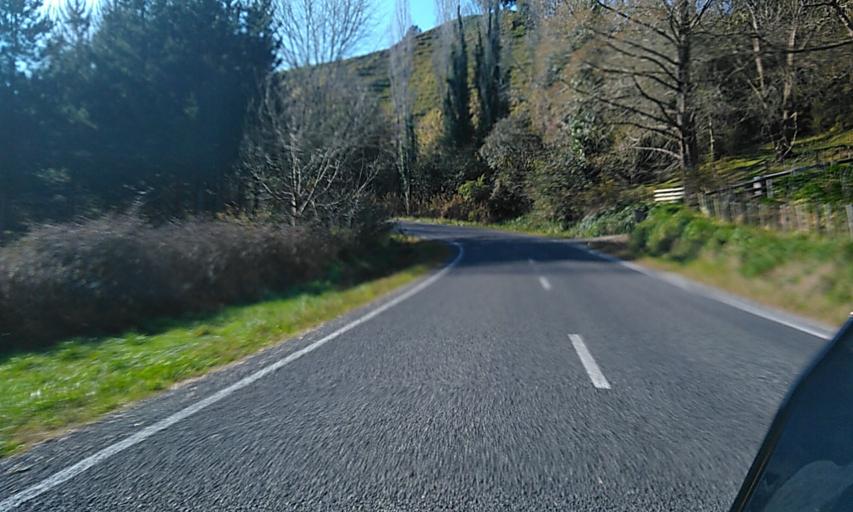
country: NZ
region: Gisborne
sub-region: Gisborne District
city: Gisborne
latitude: -38.5624
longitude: 178.0246
